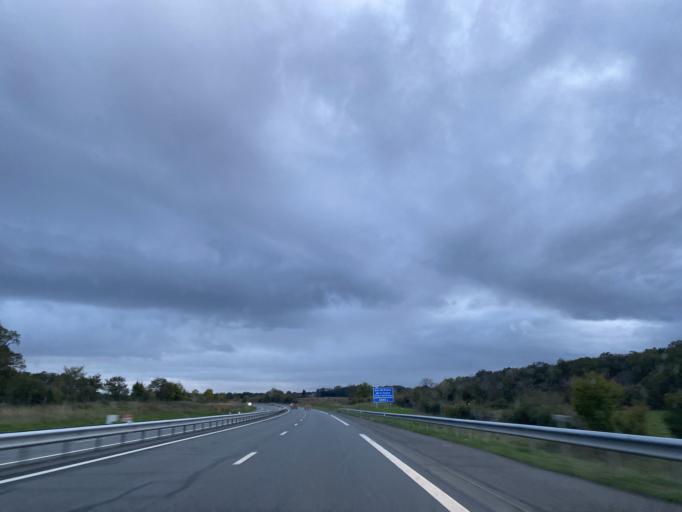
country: FR
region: Centre
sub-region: Departement du Cher
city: Orval
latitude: 46.7747
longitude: 2.4062
